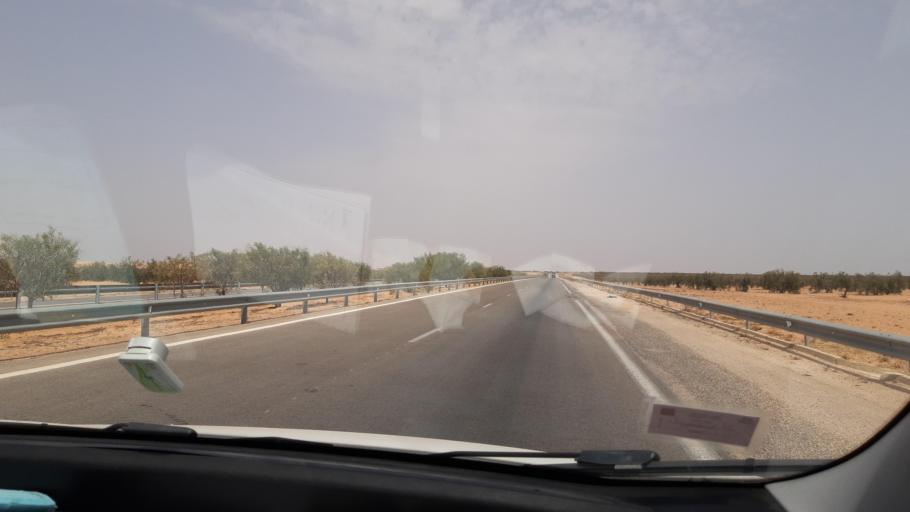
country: TN
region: Safaqis
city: Bi'r `Ali Bin Khalifah
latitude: 34.5563
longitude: 10.3326
